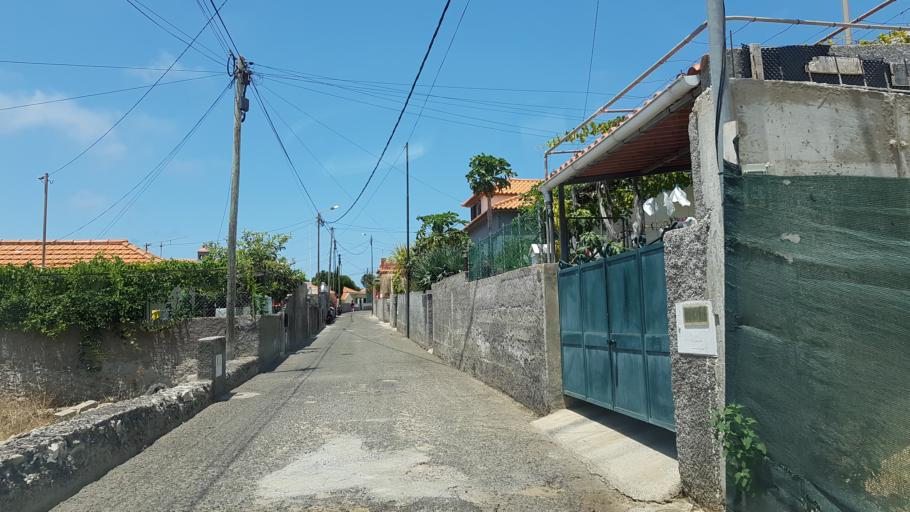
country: PT
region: Madeira
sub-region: Porto Santo
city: Vila de Porto Santo
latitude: 33.0704
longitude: -16.3398
